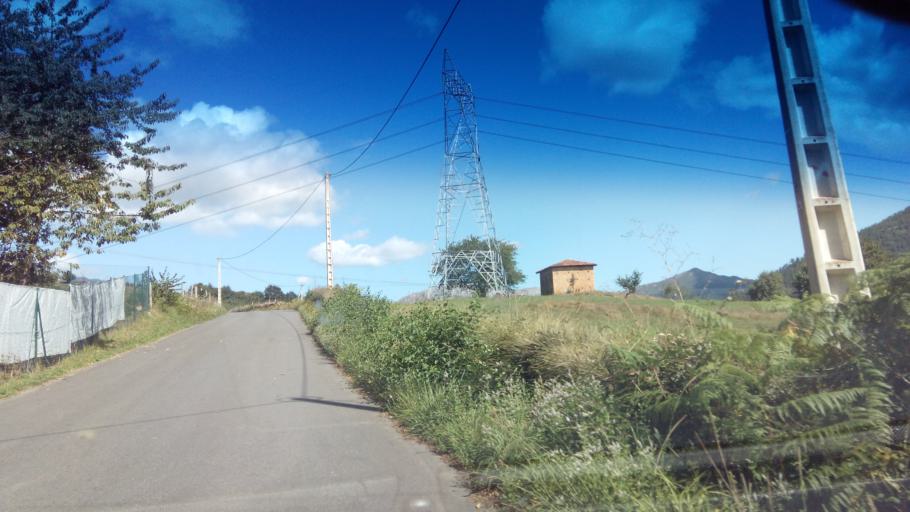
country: ES
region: Asturias
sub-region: Province of Asturias
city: Parres
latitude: 43.3706
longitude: -5.1718
